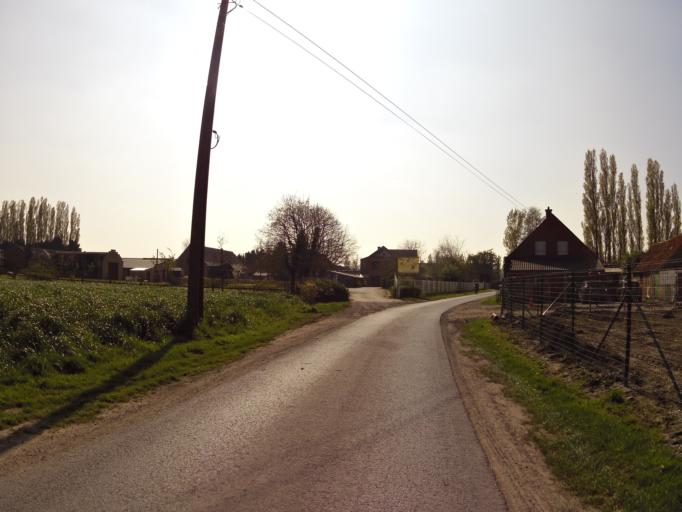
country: BE
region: Flanders
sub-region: Provincie West-Vlaanderen
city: Gistel
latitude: 51.1276
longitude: 2.9857
